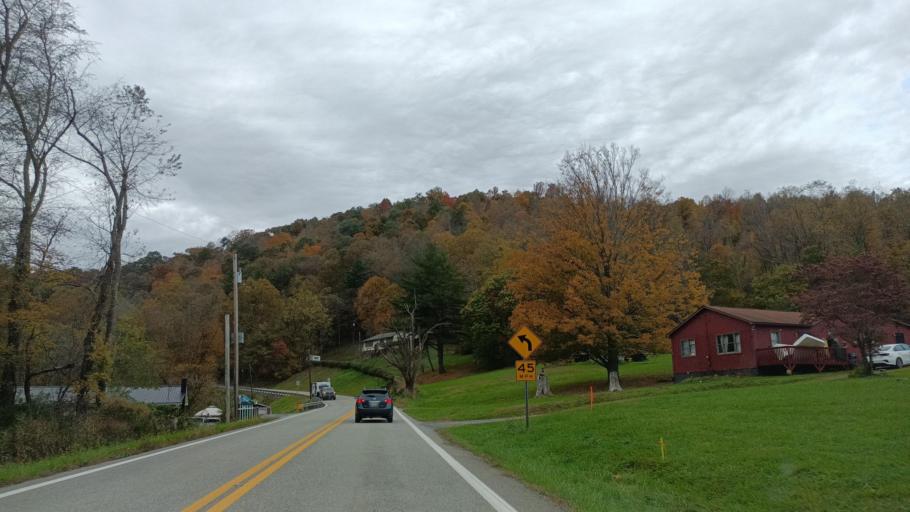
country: US
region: West Virginia
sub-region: Taylor County
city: Grafton
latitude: 39.3445
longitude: -79.9511
